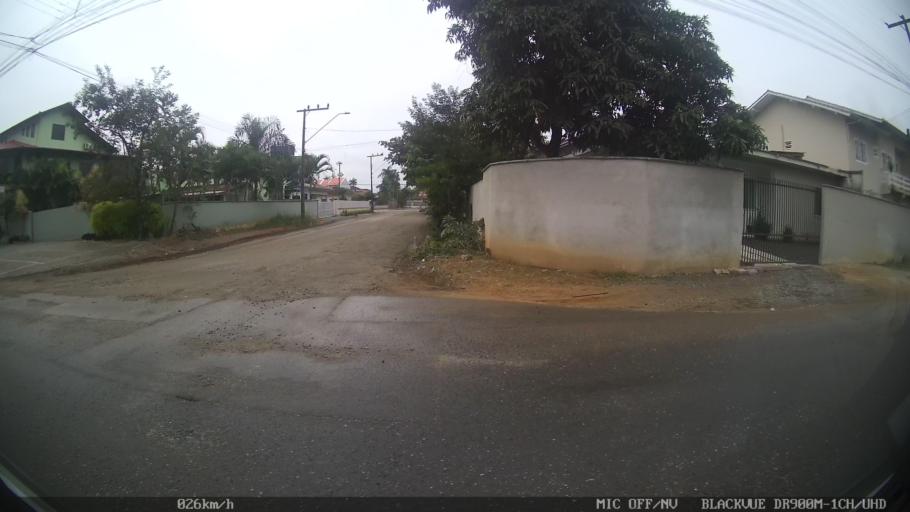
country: BR
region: Santa Catarina
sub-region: Joinville
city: Joinville
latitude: -26.2356
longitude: -48.8141
